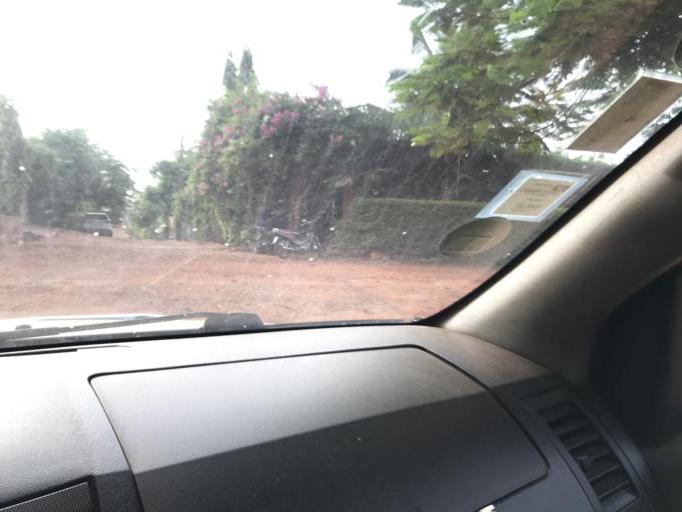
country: ML
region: Bamako
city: Bamako
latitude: 12.5878
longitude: -8.0062
